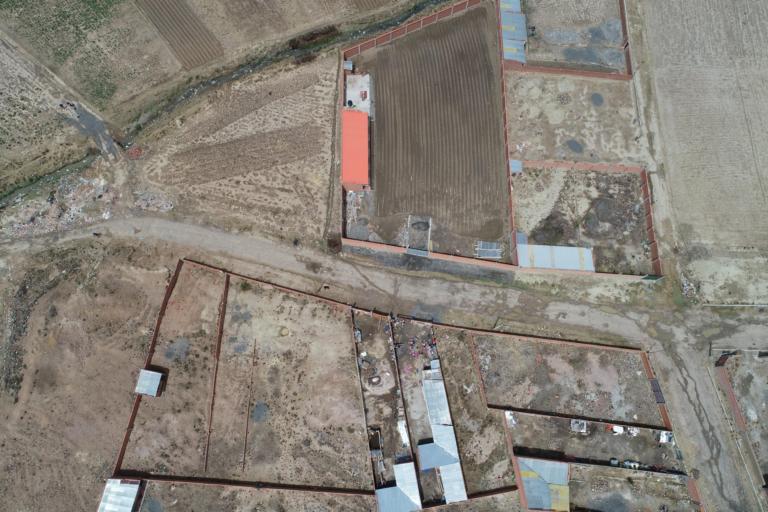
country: BO
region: La Paz
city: Achacachi
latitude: -16.0541
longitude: -68.6826
